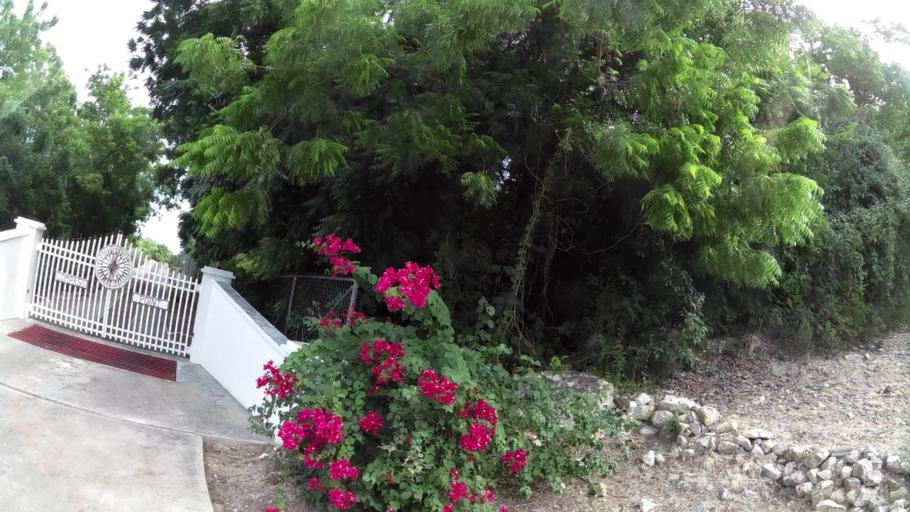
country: AG
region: Saint Peter
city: Parham
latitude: 17.0688
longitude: -61.6988
